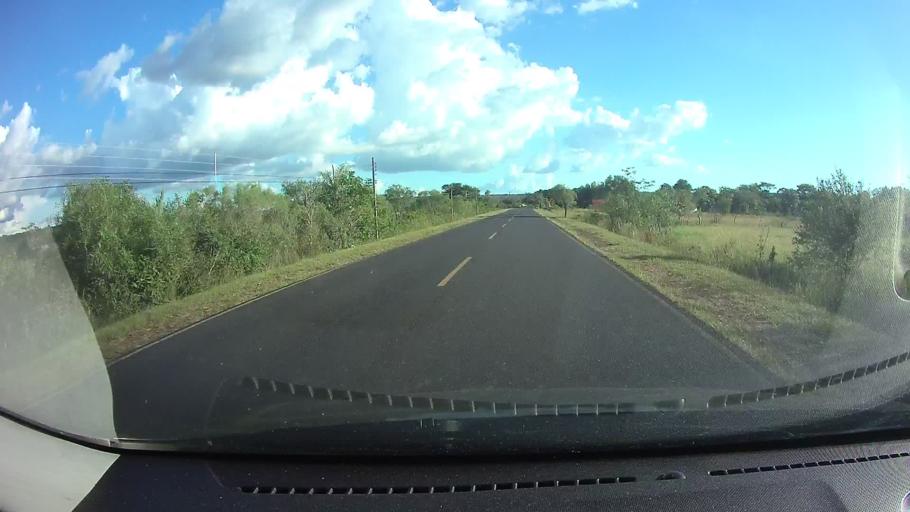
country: PY
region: Cordillera
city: Emboscada
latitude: -25.1506
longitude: -57.2609
